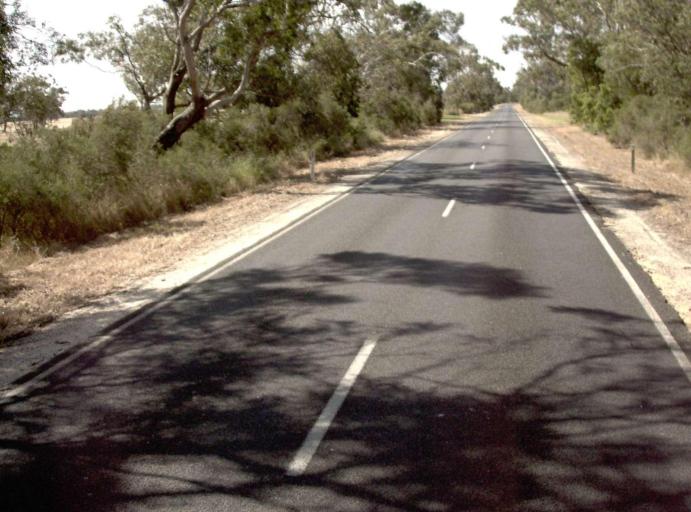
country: AU
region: Victoria
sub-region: Wellington
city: Sale
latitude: -38.3113
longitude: 147.1539
